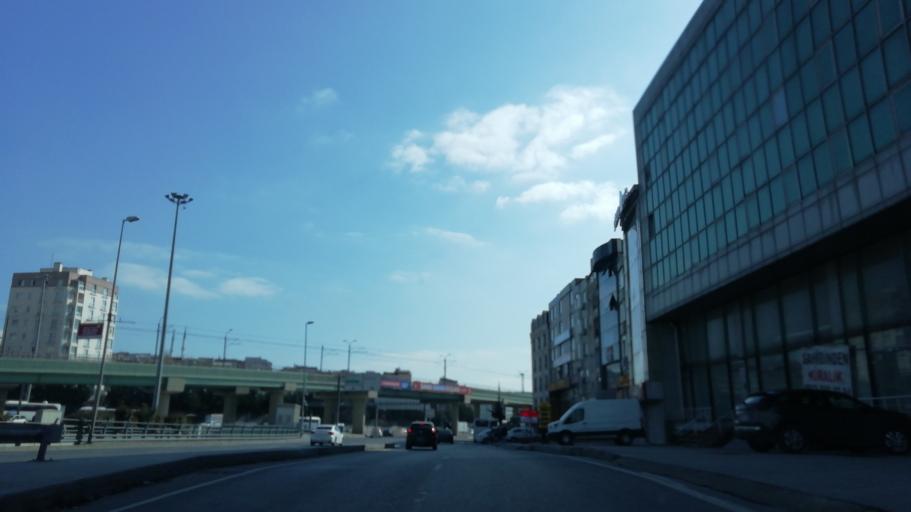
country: TR
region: Istanbul
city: Esenler
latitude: 41.0359
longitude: 28.8931
